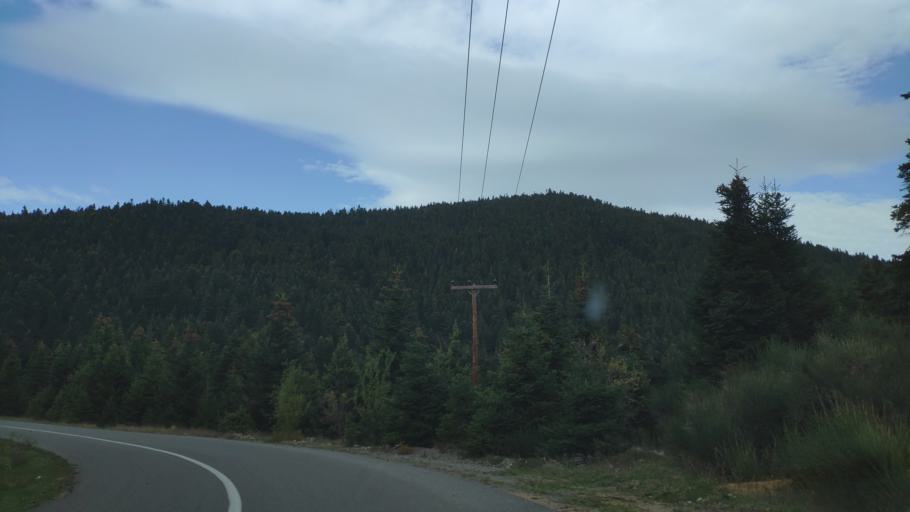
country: GR
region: Central Greece
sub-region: Nomos Fokidos
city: Amfissa
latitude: 38.7085
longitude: 22.3257
